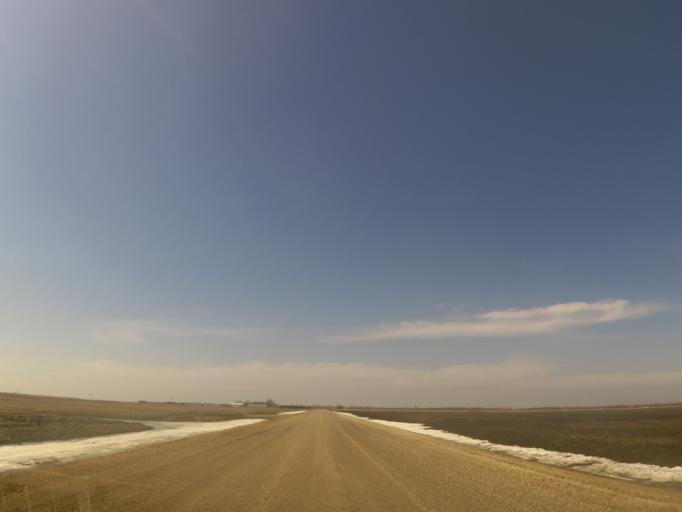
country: US
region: North Dakota
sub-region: Walsh County
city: Grafton
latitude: 48.4265
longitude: -97.2496
